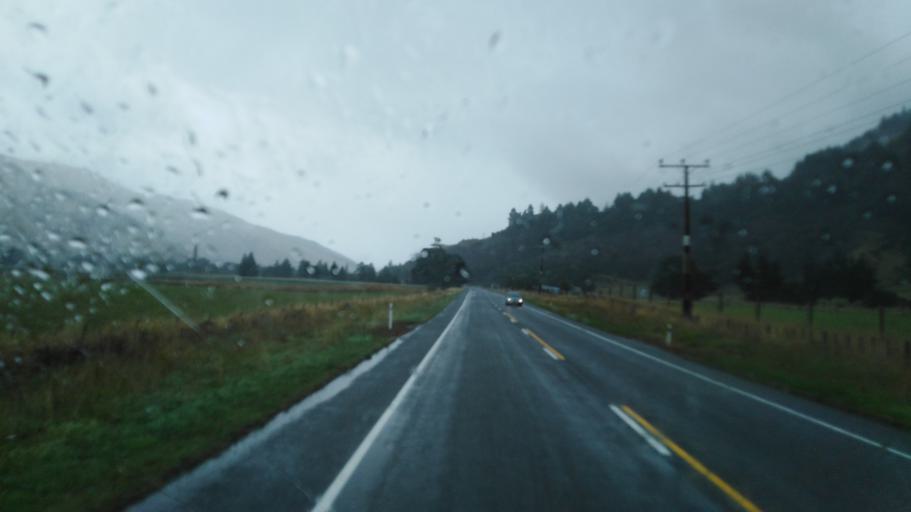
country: NZ
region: Marlborough
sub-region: Marlborough District
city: Picton
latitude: -41.3257
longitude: 173.7635
